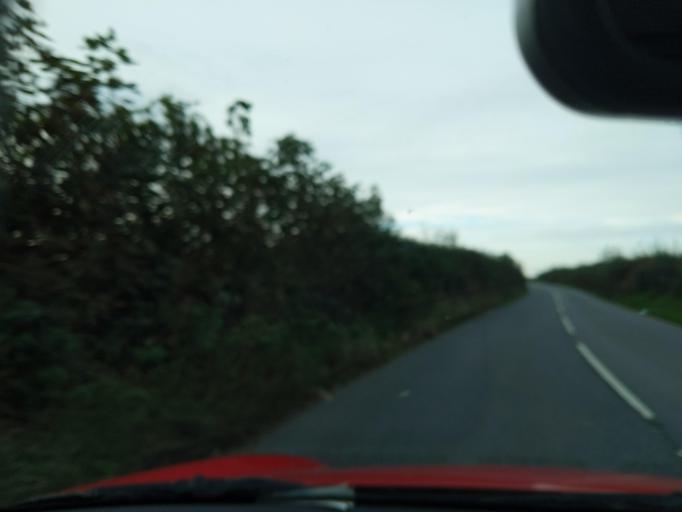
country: GB
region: England
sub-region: Devon
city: Great Torrington
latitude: 50.9136
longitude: -4.1399
